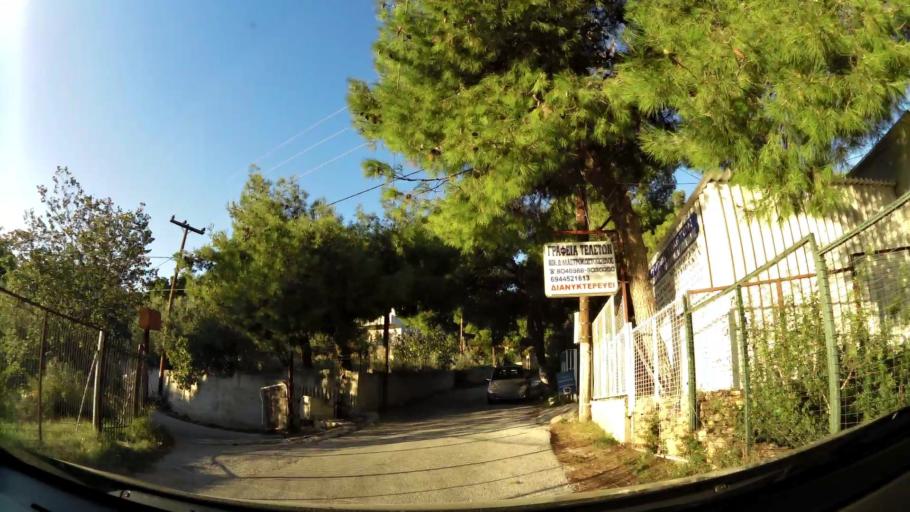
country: GR
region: Attica
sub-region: Nomarchia Athinas
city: Penteli
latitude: 38.0428
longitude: 23.8607
